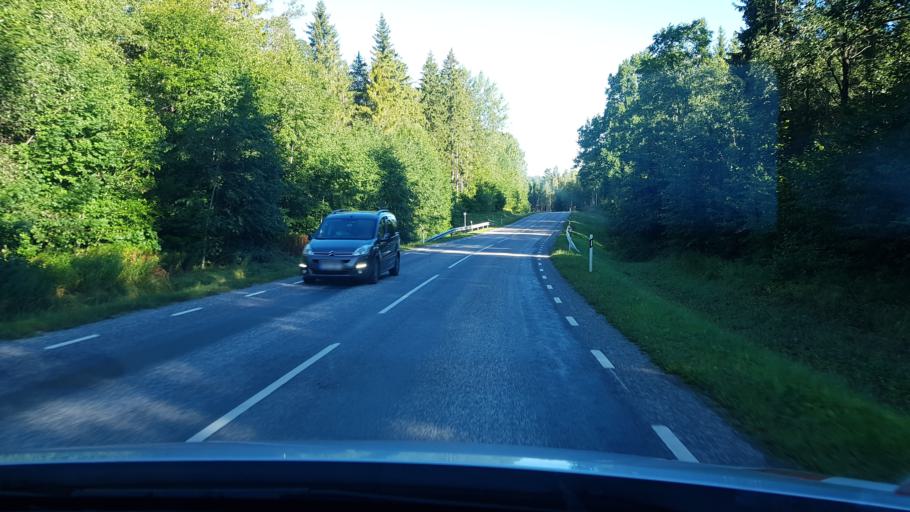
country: EE
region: Vorumaa
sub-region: Antsla vald
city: Vana-Antsla
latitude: 58.0259
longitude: 26.5783
